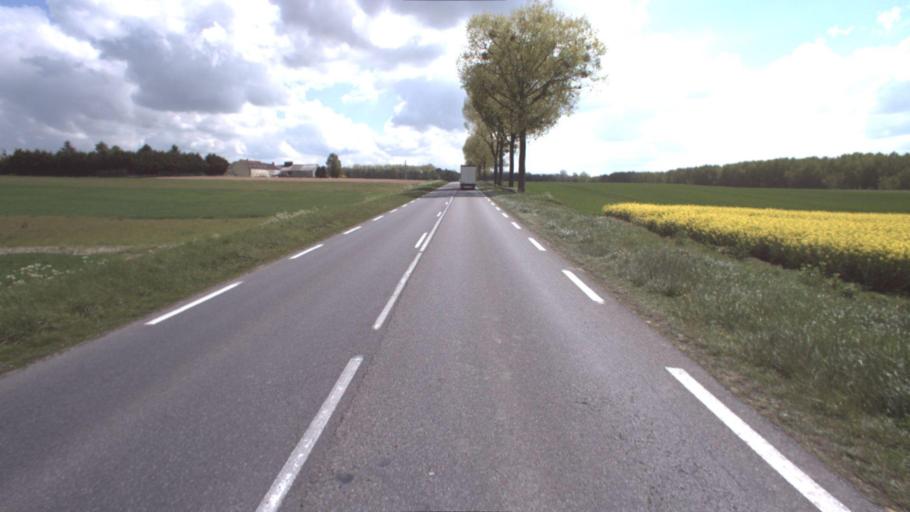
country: FR
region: Ile-de-France
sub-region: Departement de Seine-et-Marne
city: La Ferte-Gaucher
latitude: 48.6946
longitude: 3.3107
